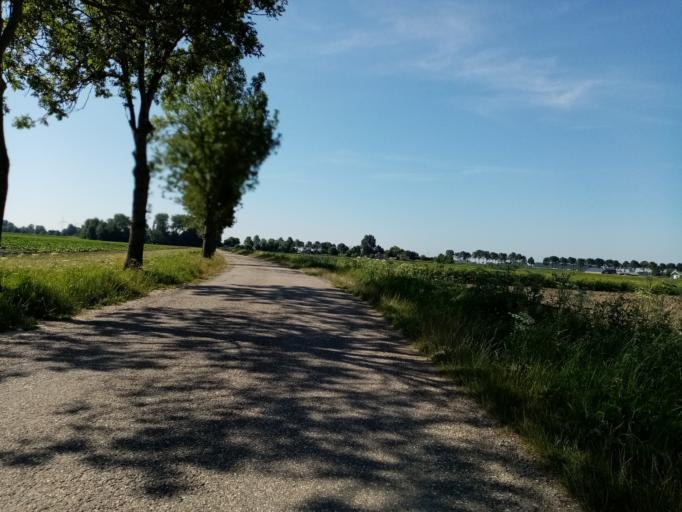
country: NL
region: North Brabant
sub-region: Gemeente Moerdijk
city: Klundert
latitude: 51.6618
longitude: 4.6323
